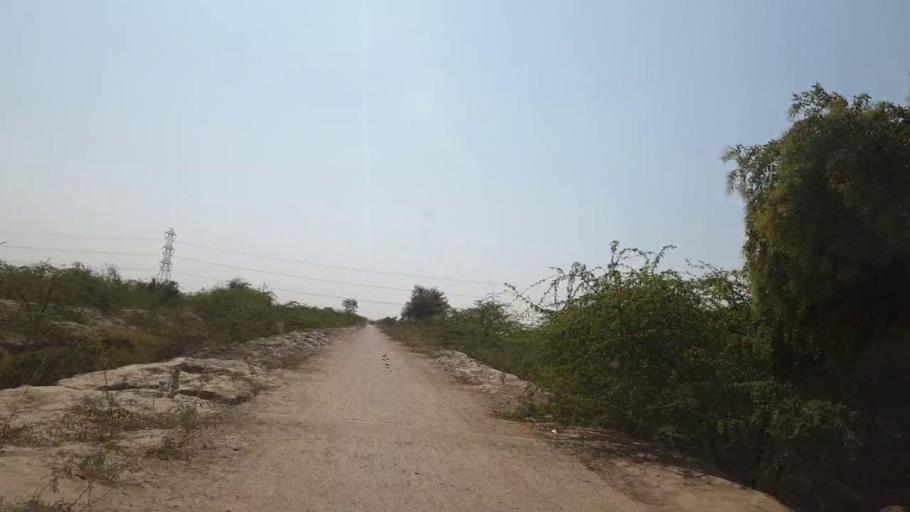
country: PK
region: Sindh
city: Nabisar
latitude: 25.0658
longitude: 69.5375
